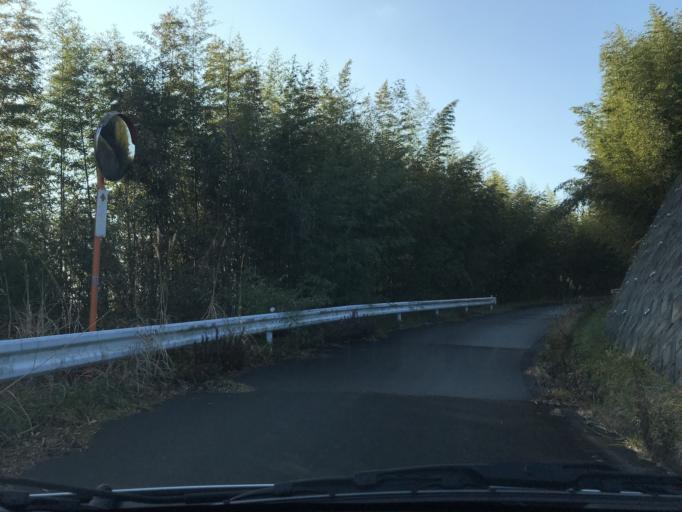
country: JP
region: Miyagi
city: Wakuya
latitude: 38.6926
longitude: 141.1151
